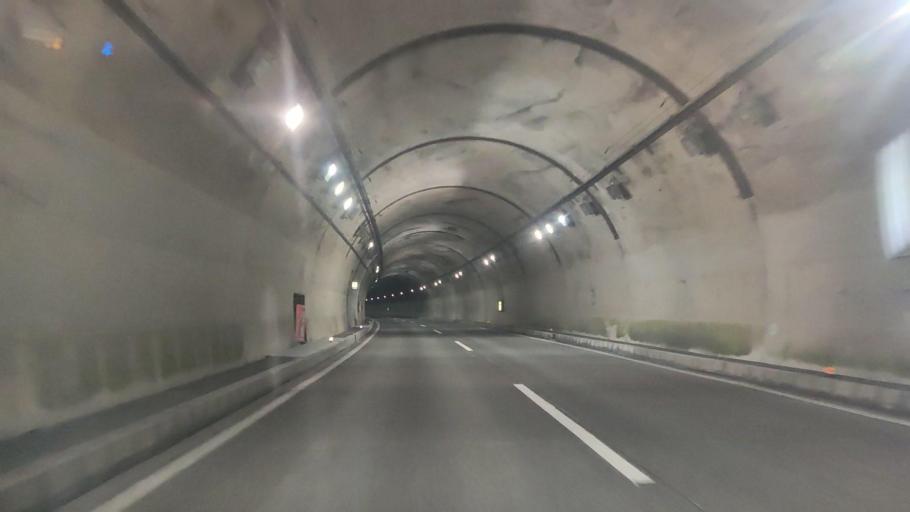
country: JP
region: Oita
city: Beppu
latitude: 33.2691
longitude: 131.3405
